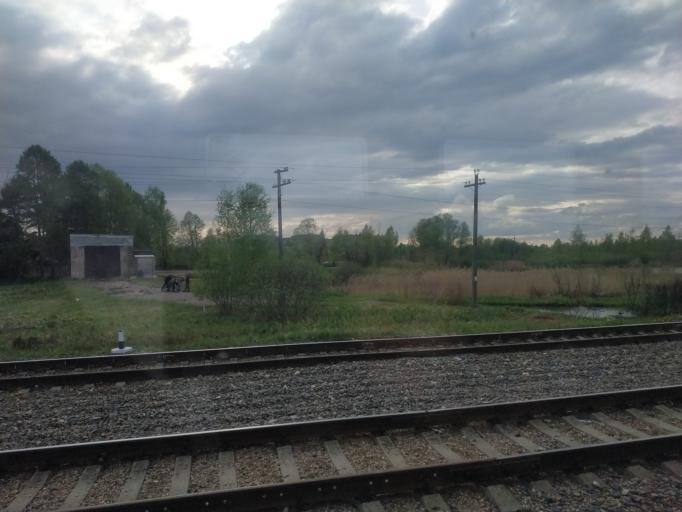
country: RU
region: Smolensk
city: Ugra
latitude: 54.7733
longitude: 34.3428
